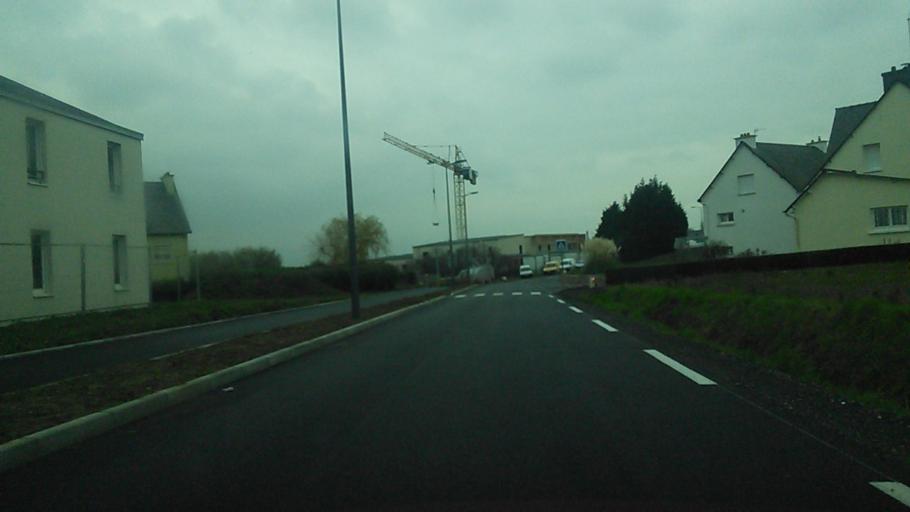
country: FR
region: Brittany
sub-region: Departement des Cotes-d'Armor
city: Yffiniac
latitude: 48.4837
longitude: -2.6615
